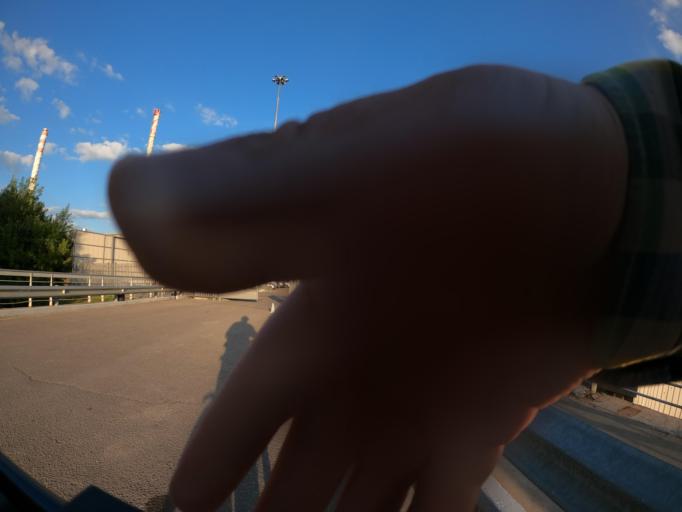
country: RU
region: Moskovskaya
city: Raduzhnyy
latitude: 55.1078
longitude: 38.7517
